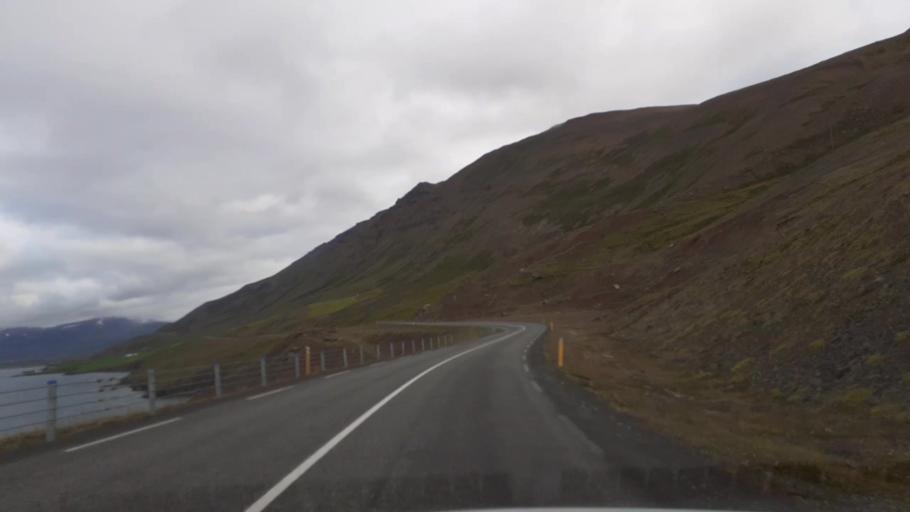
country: IS
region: Northeast
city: Akureyri
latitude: 65.8317
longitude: -18.0574
